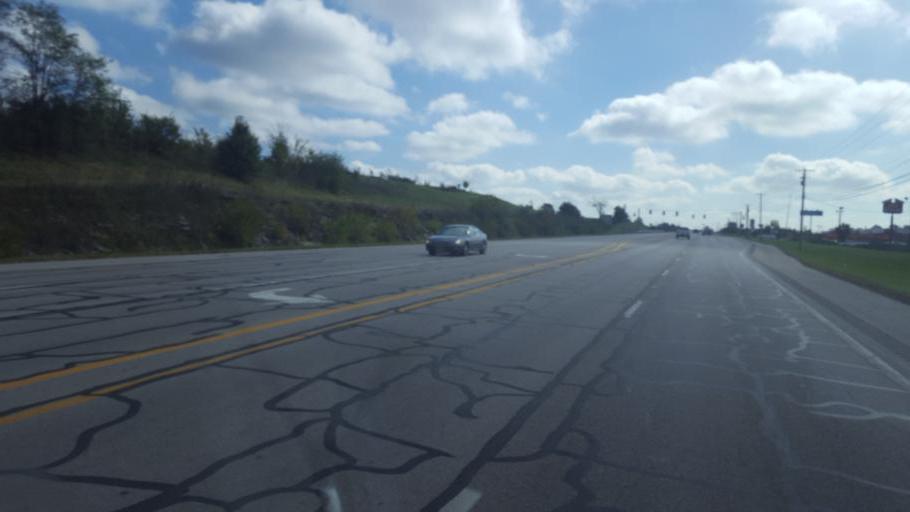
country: US
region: Ohio
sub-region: Brown County
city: Aberdeen
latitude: 38.6244
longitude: -83.7873
